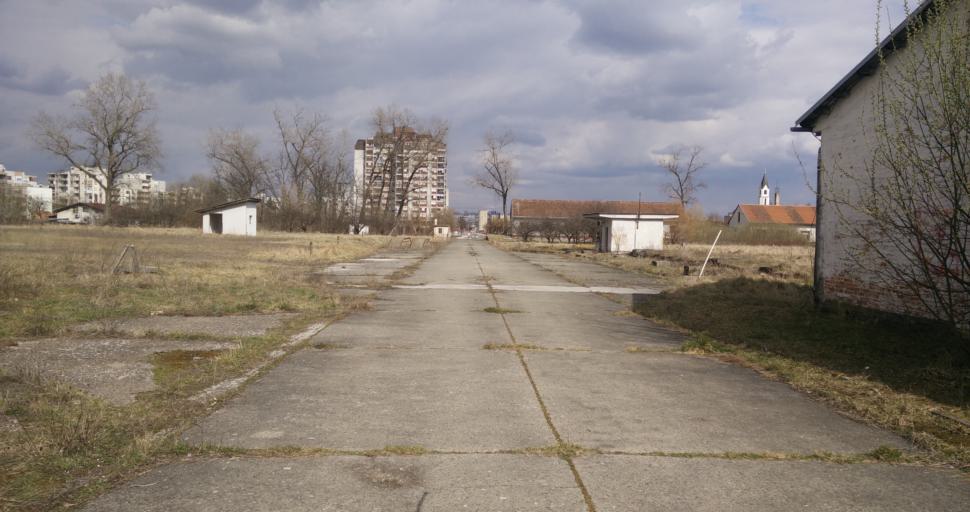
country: HR
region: Karlovacka
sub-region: Grad Karlovac
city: Karlovac
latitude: 45.4852
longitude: 15.5389
